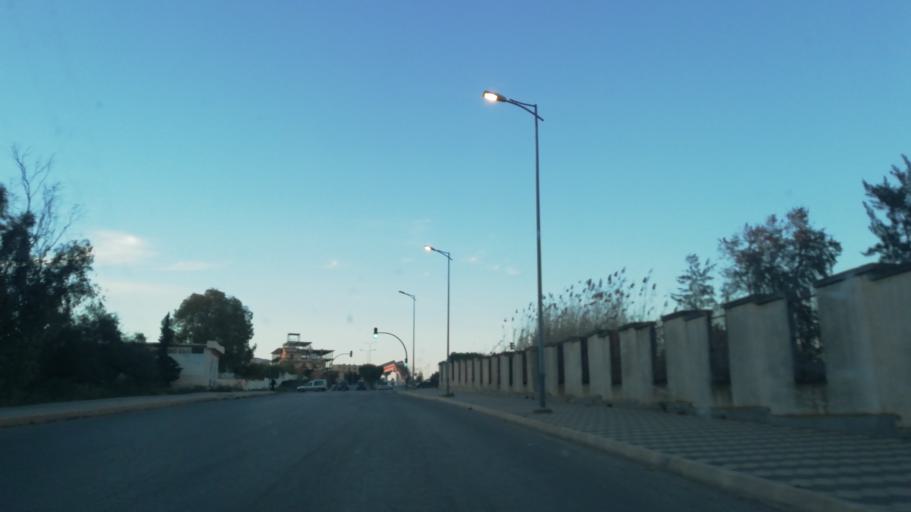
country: DZ
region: Oran
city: Bir el Djir
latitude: 35.7080
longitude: -0.5856
